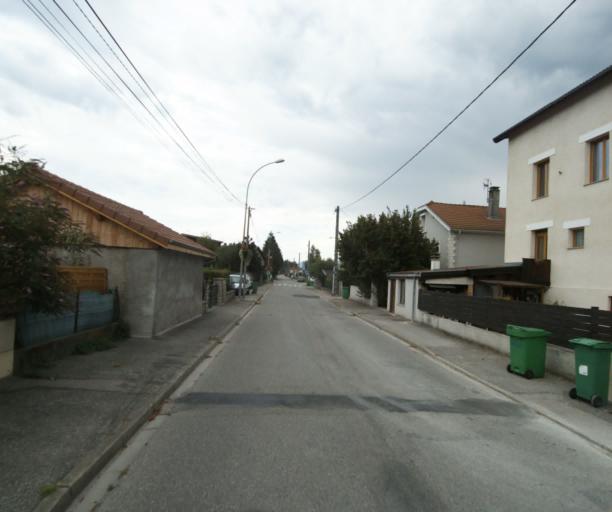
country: FR
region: Rhone-Alpes
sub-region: Departement de l'Isere
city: Domene
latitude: 45.1967
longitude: 5.8232
